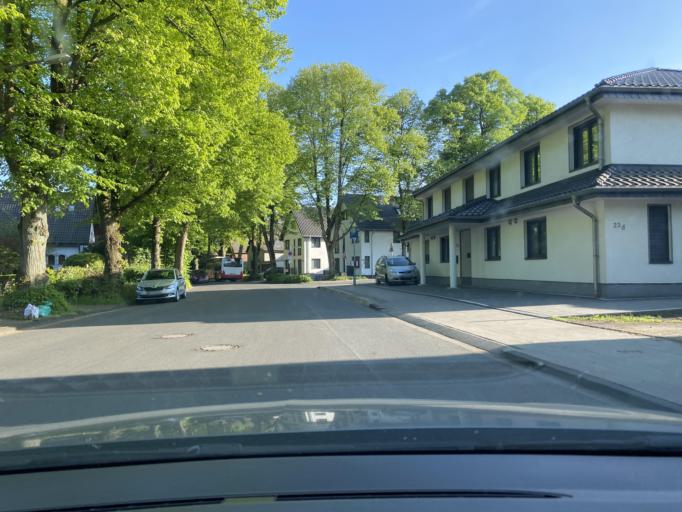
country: DE
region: North Rhine-Westphalia
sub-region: Regierungsbezirk Dusseldorf
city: Moers
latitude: 51.4860
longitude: 6.6677
